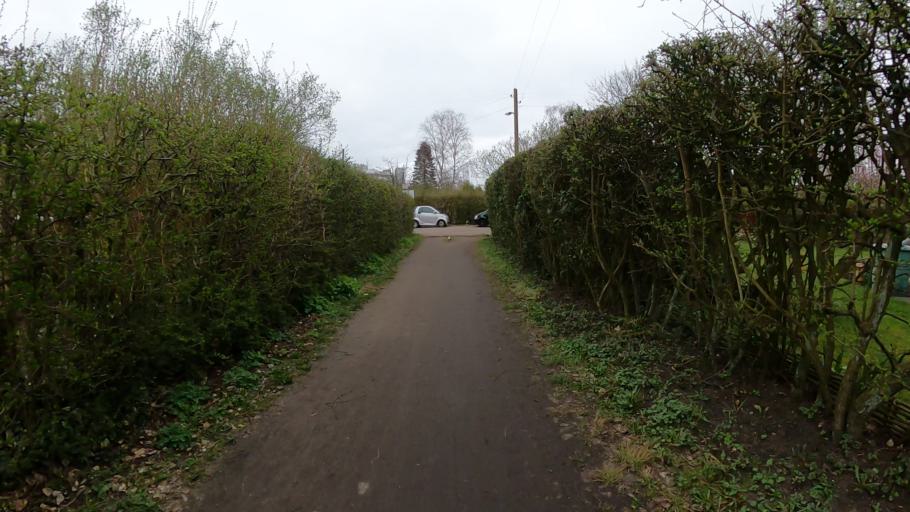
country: DE
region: Hamburg
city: Winterhude
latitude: 53.6184
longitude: 9.9770
